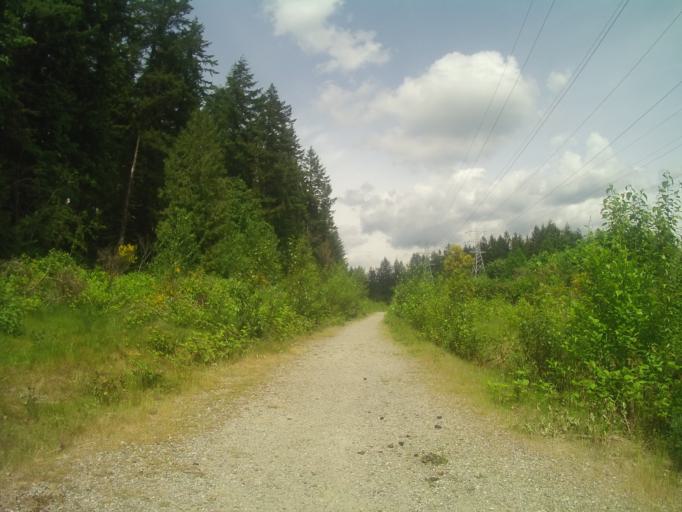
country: CA
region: British Columbia
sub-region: Fraser Valley Regional District
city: North Vancouver
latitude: 49.3167
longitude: -123.0176
